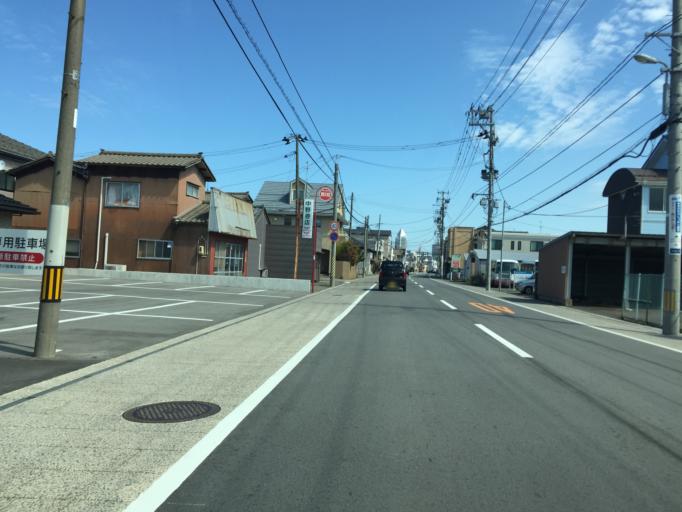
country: JP
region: Niigata
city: Niigata-shi
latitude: 37.9116
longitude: 139.0278
